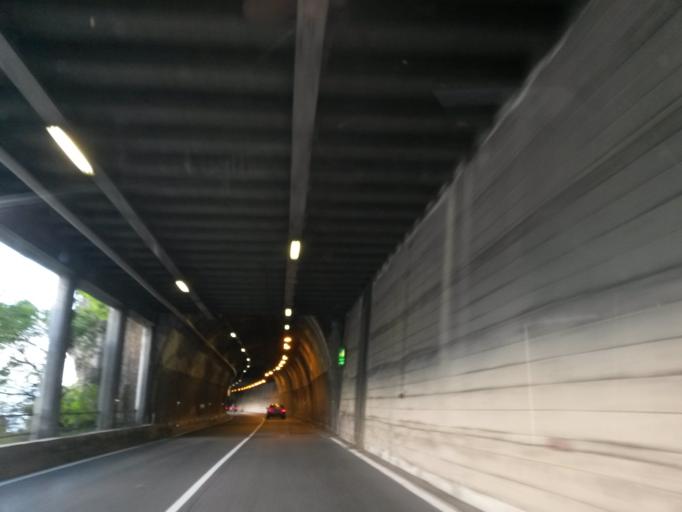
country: IT
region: Lombardy
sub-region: Provincia di Brescia
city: Limone sul Garda
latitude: 45.7938
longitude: 10.7812
